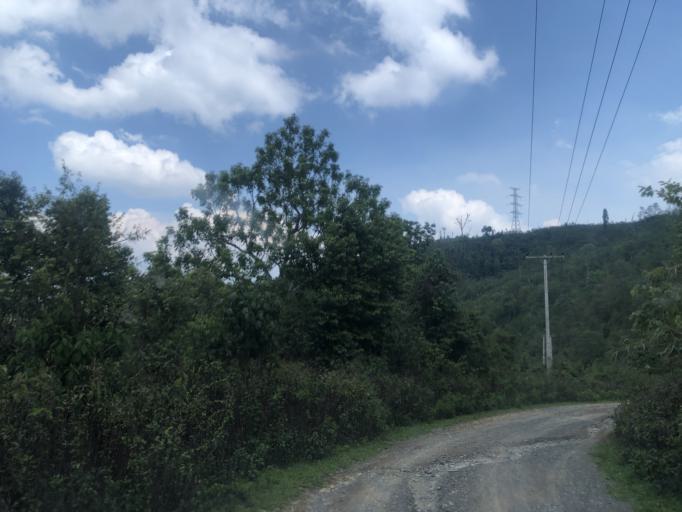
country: LA
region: Phongsali
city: Phongsali
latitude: 21.3899
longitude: 102.1974
